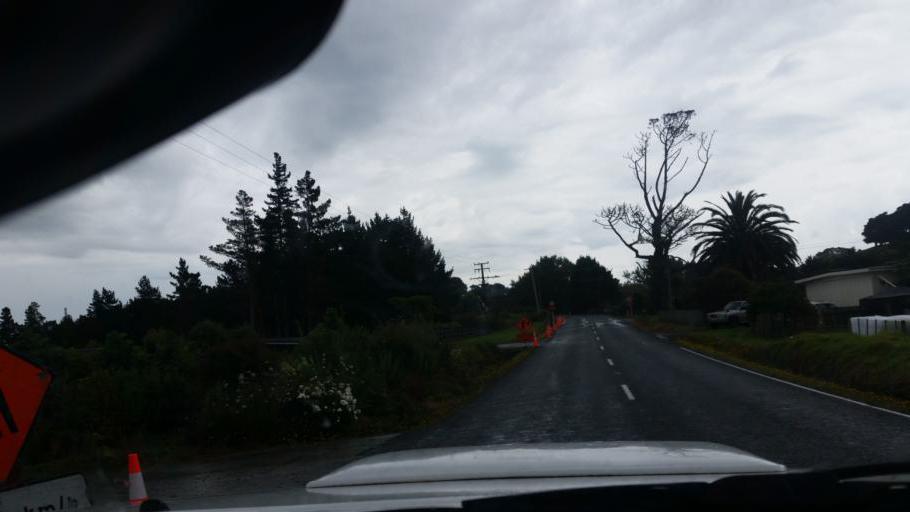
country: NZ
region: Auckland
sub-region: Auckland
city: Wellsford
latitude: -36.1518
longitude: 174.2215
